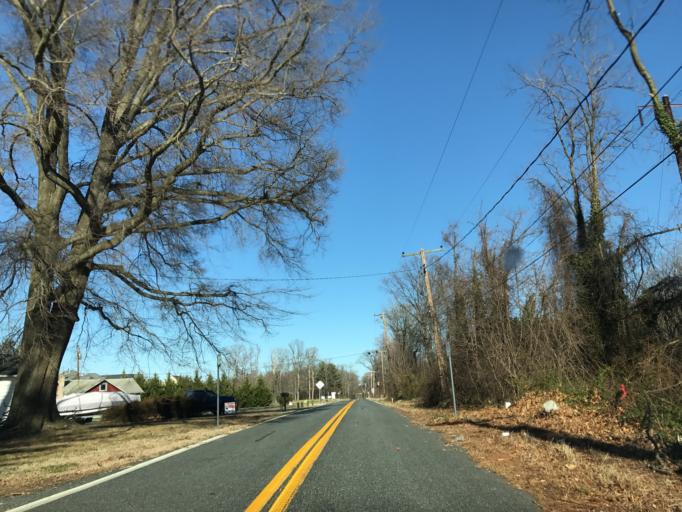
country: US
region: Maryland
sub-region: Harford County
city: Riverside
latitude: 39.4399
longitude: -76.2376
